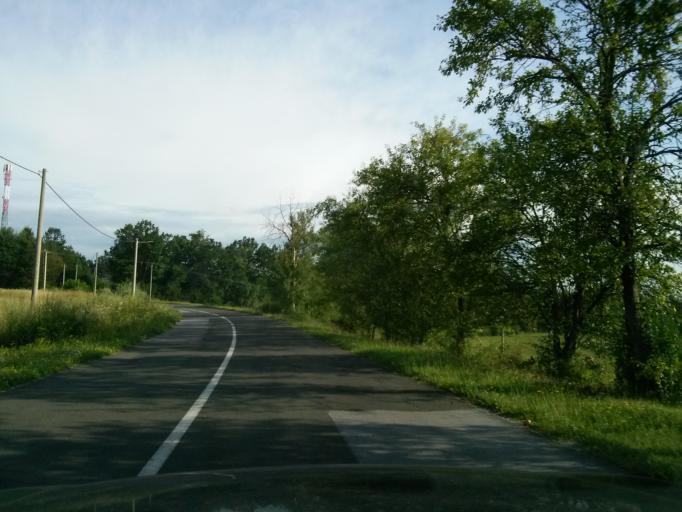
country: HR
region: Sisacko-Moslavacka
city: Gvozd
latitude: 45.5186
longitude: 15.8860
